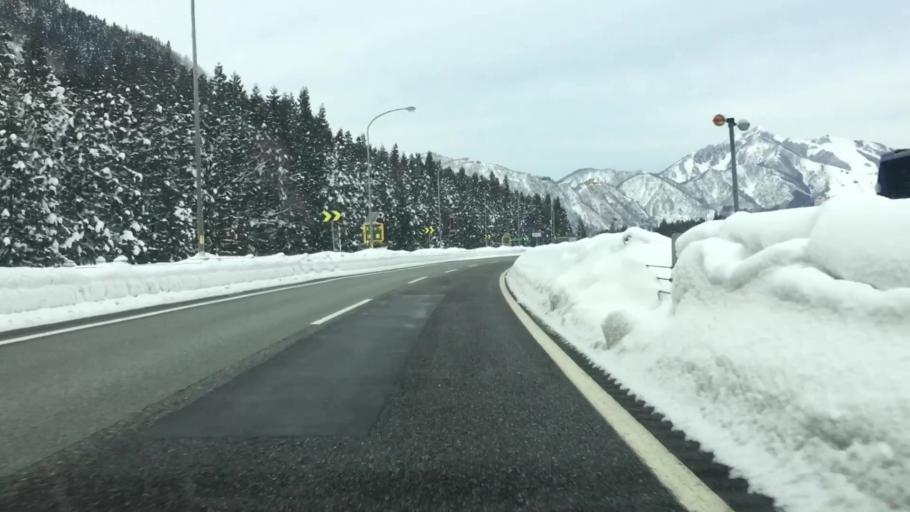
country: JP
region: Niigata
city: Shiozawa
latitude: 36.8929
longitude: 138.8460
